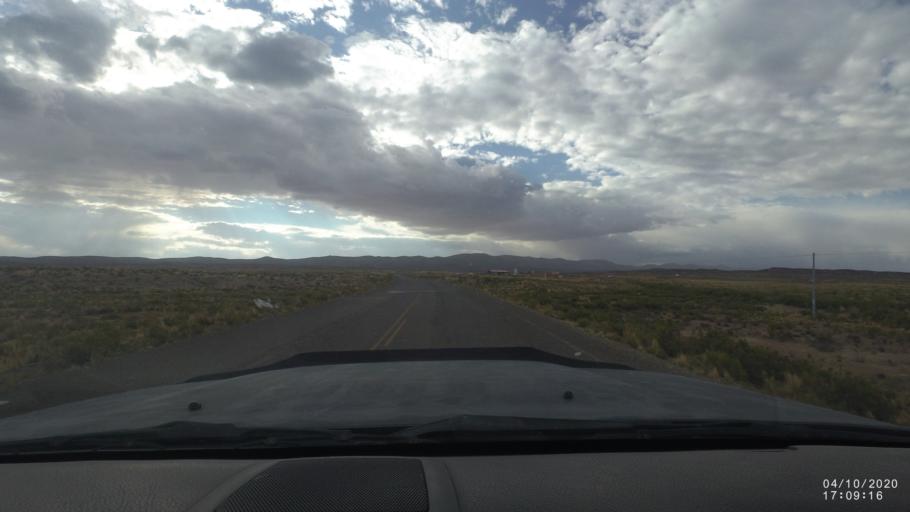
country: BO
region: Oruro
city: Oruro
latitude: -18.3402
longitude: -67.5811
